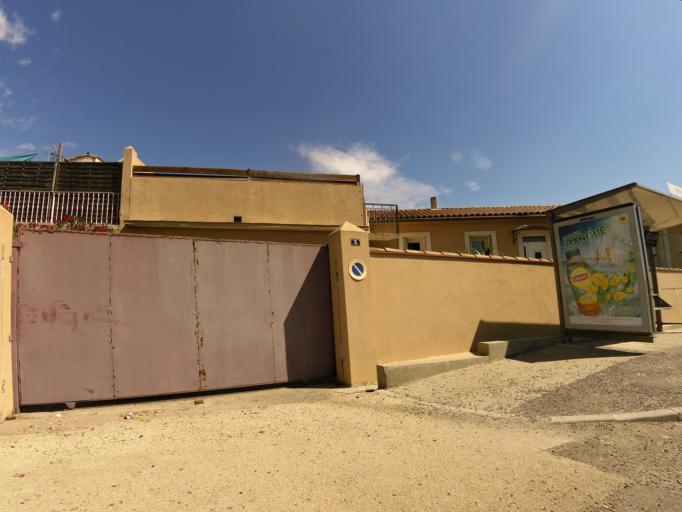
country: FR
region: Languedoc-Roussillon
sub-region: Departement de l'Herault
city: Vendargues
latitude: 43.6538
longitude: 3.9686
